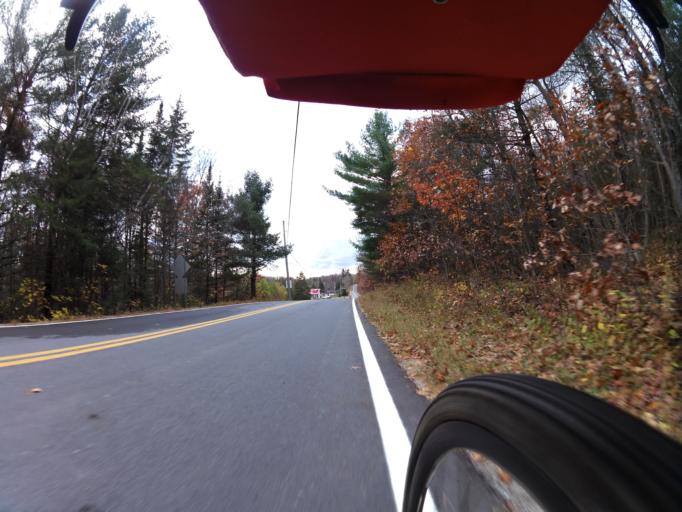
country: CA
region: Quebec
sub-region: Outaouais
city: Shawville
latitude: 45.6832
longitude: -76.2256
